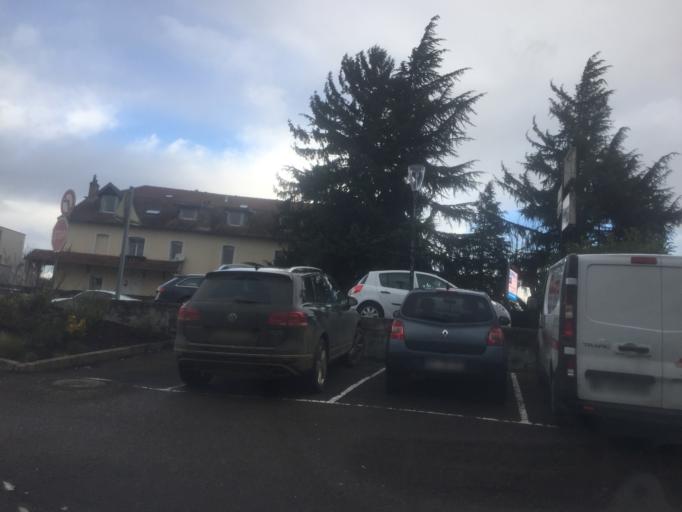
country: FR
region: Franche-Comte
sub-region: Departement du Doubs
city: Saint-Vit
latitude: 47.1824
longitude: 5.8128
